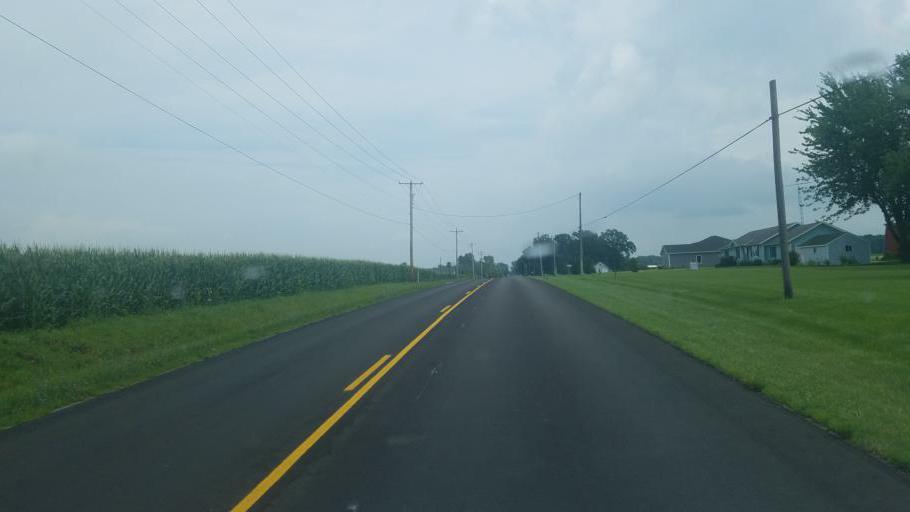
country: US
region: Ohio
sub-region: Logan County
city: Russells Point
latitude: 40.4706
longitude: -83.8502
